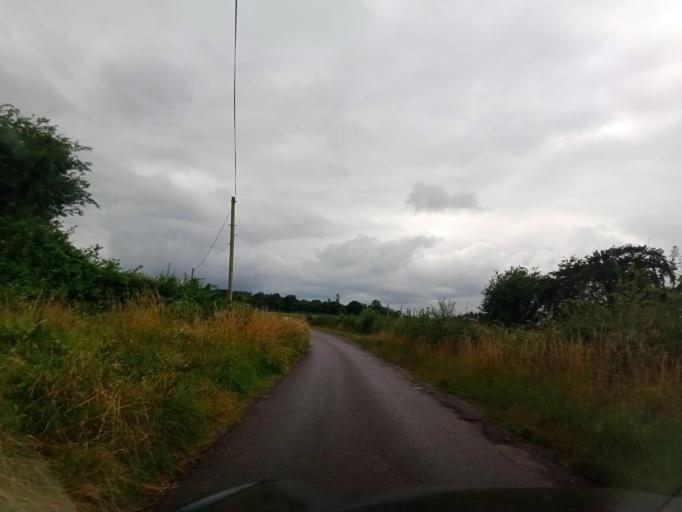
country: IE
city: Ballylinan
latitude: 52.9235
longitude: -7.0631
